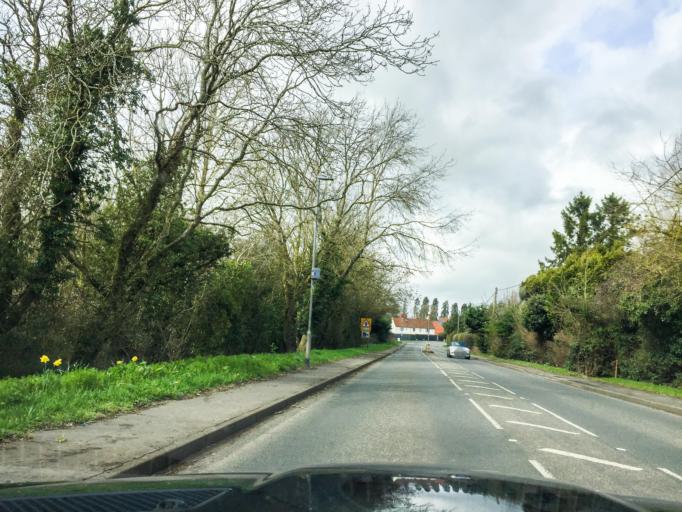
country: GB
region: England
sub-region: Warwickshire
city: Harbury
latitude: 52.1821
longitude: -1.4644
